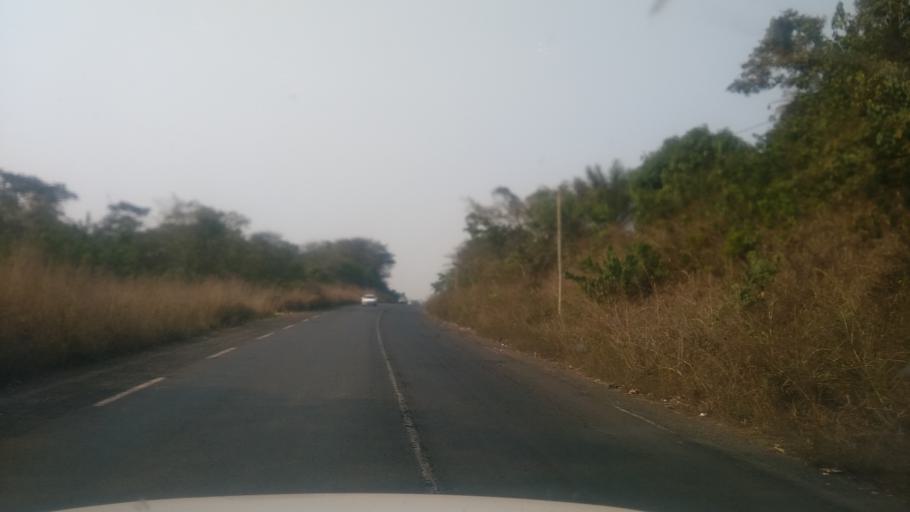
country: CM
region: West
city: Tonga
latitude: 5.0464
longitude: 10.6999
